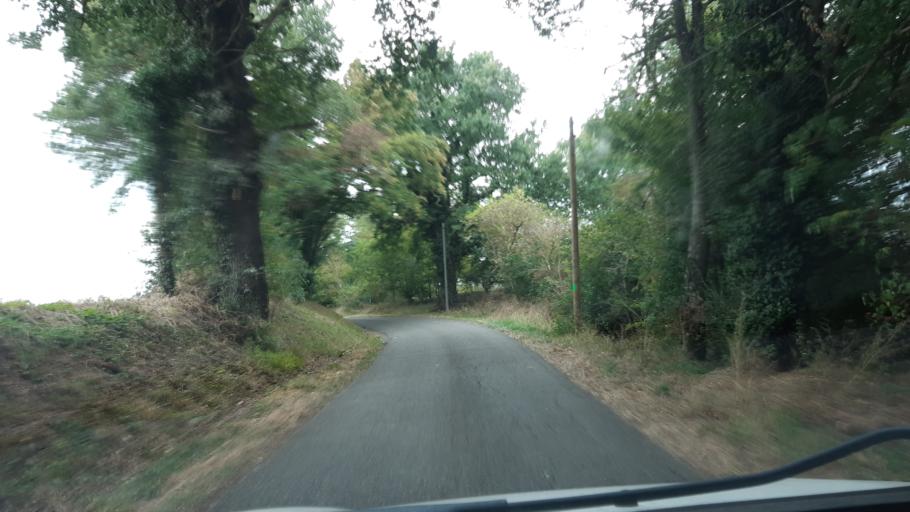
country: FR
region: Midi-Pyrenees
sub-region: Departement du Gers
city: Gimont
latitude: 43.6987
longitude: 0.9777
